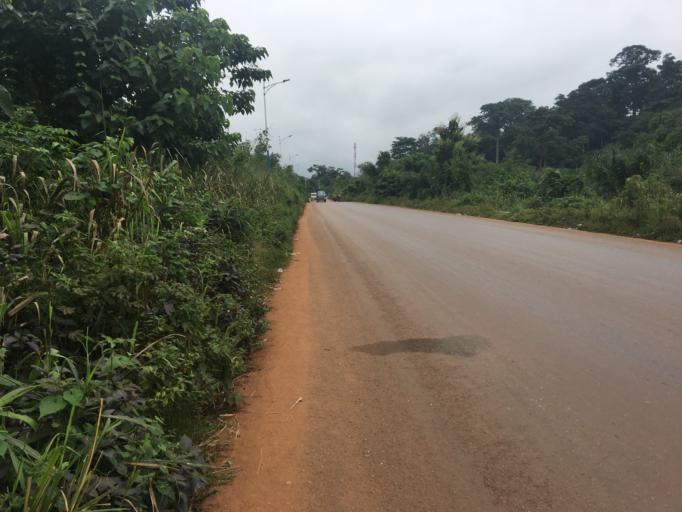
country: GH
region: Western
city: Bibiani
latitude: 6.8091
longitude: -2.5088
